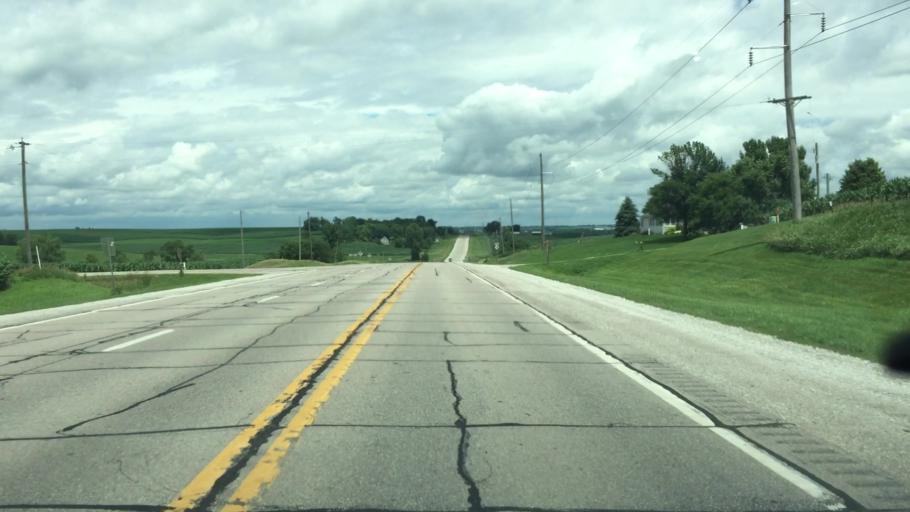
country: US
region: Iowa
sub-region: Jasper County
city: Monroe
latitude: 41.5800
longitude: -93.0971
